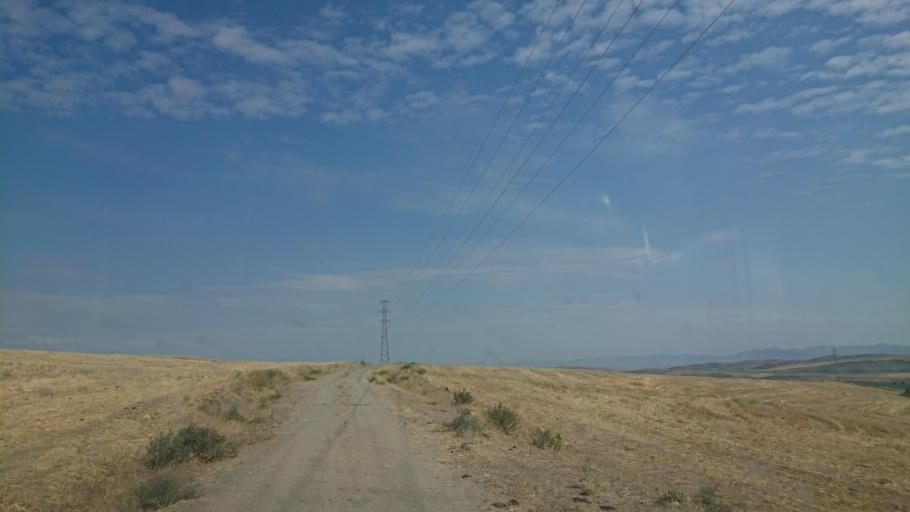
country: TR
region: Aksaray
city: Agacoren
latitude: 38.9493
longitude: 33.9122
